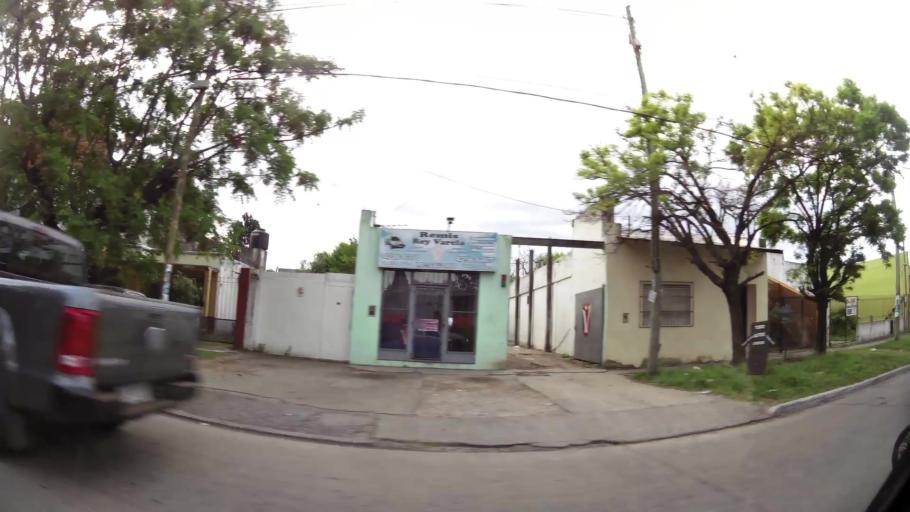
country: AR
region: Buenos Aires
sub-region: Partido de Quilmes
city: Quilmes
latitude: -34.7531
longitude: -58.2287
